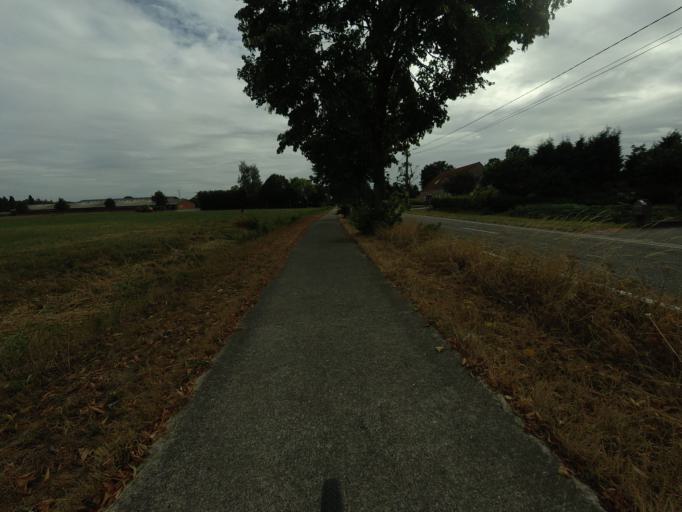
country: BE
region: Flanders
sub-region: Provincie Antwerpen
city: Brecht
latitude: 51.3351
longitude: 4.6356
